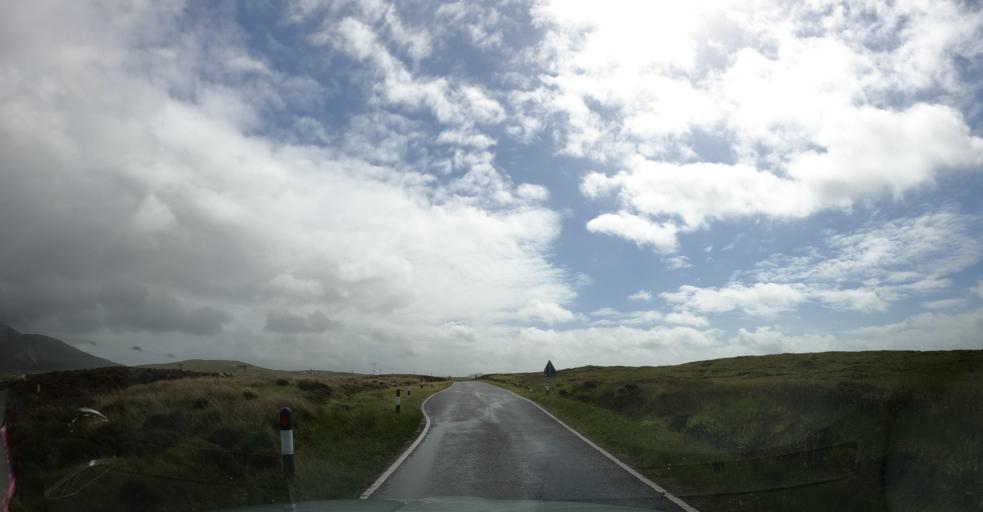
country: GB
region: Scotland
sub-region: Eilean Siar
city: Isle of South Uist
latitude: 57.2765
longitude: -7.3660
